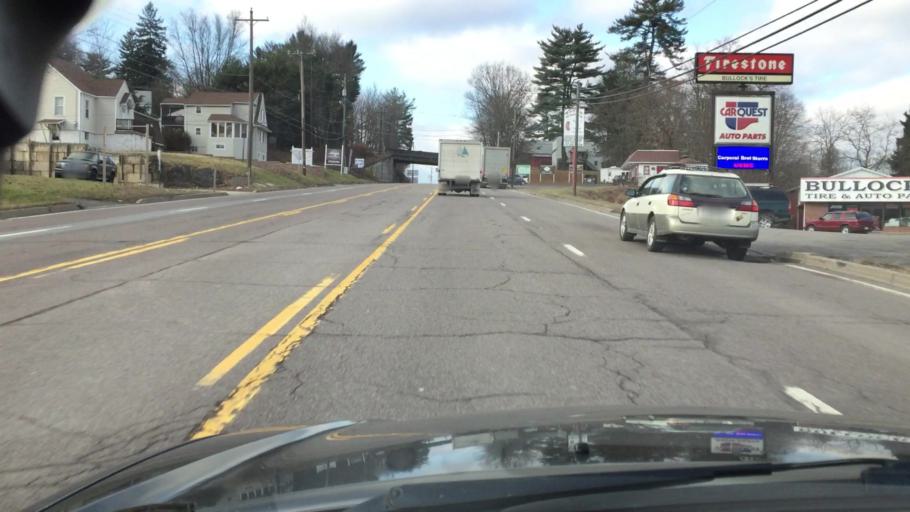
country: US
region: Pennsylvania
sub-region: Luzerne County
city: Shavertown
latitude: 41.3245
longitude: -75.9439
